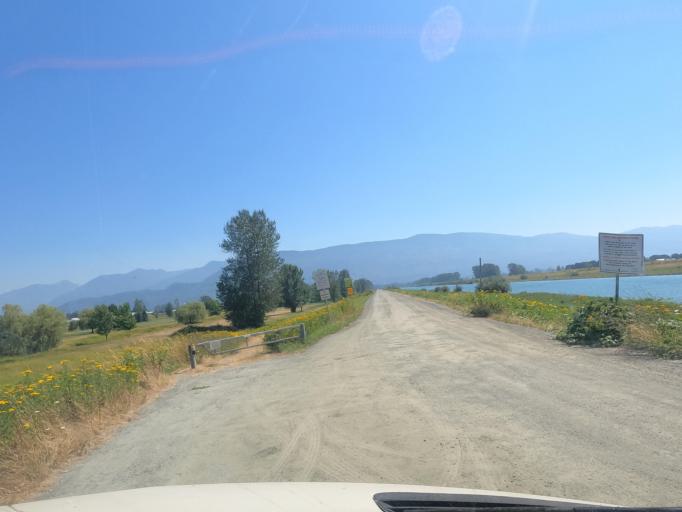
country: CA
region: British Columbia
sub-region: Fraser Valley Regional District
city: Chilliwack
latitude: 49.1226
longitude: -122.0942
